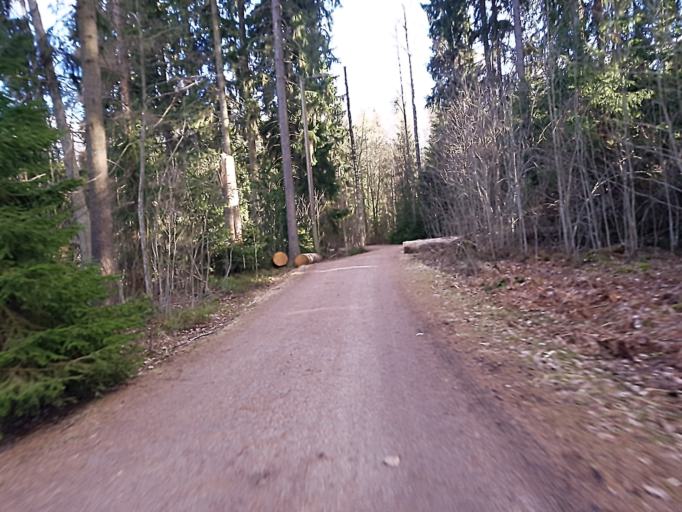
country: FI
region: Uusimaa
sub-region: Helsinki
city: Helsinki
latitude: 60.2618
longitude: 24.9285
